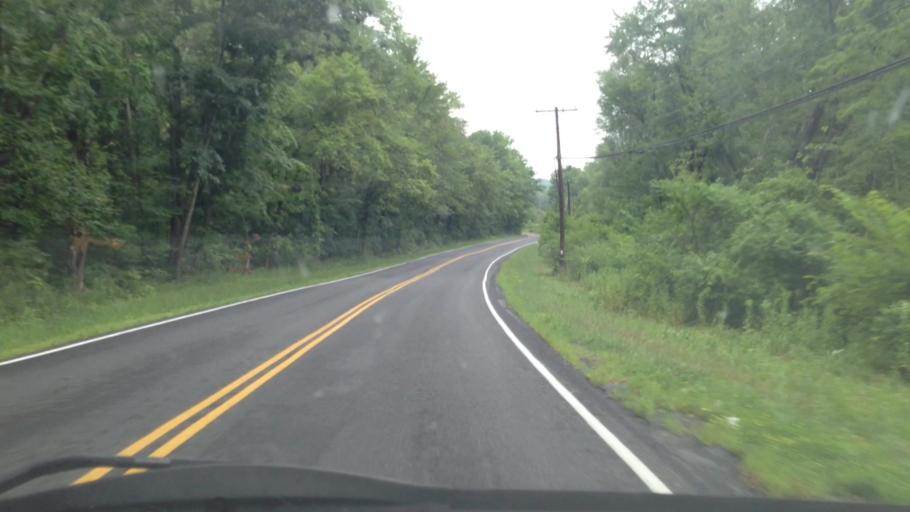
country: US
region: New York
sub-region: Ulster County
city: Highland
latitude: 41.7330
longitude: -73.9906
